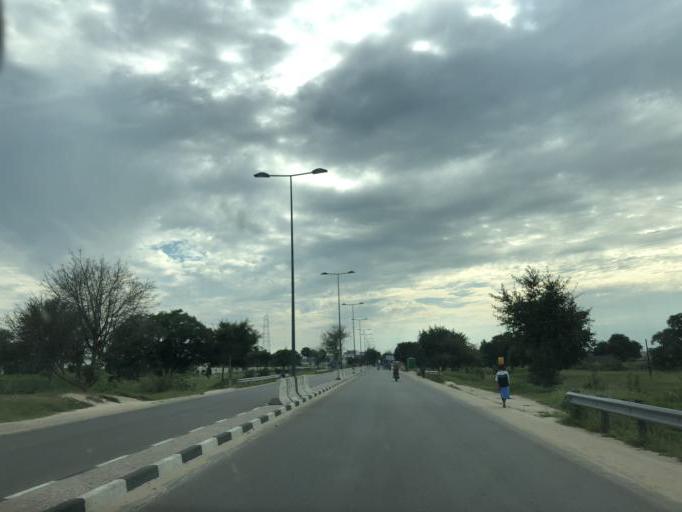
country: AO
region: Cunene
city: Ondjiva
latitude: -17.0696
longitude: 15.7176
